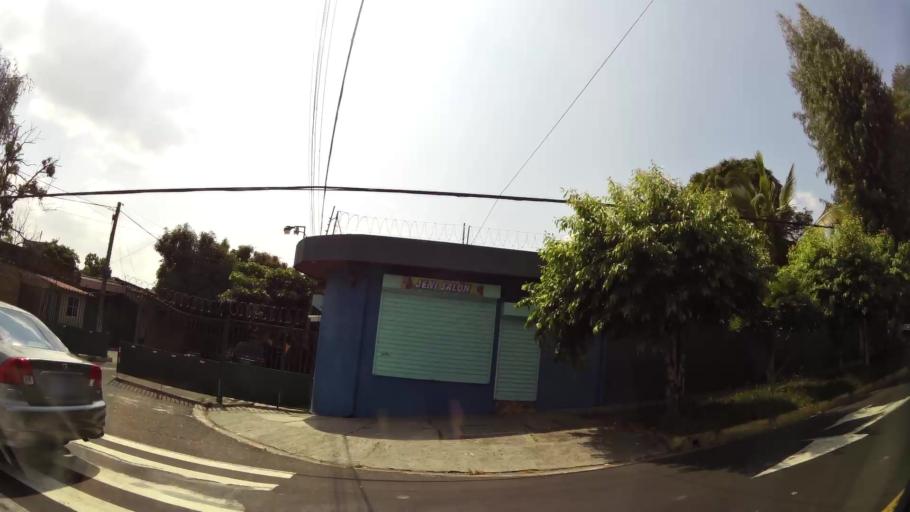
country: SV
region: San Salvador
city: Mejicanos
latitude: 13.7134
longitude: -89.2182
